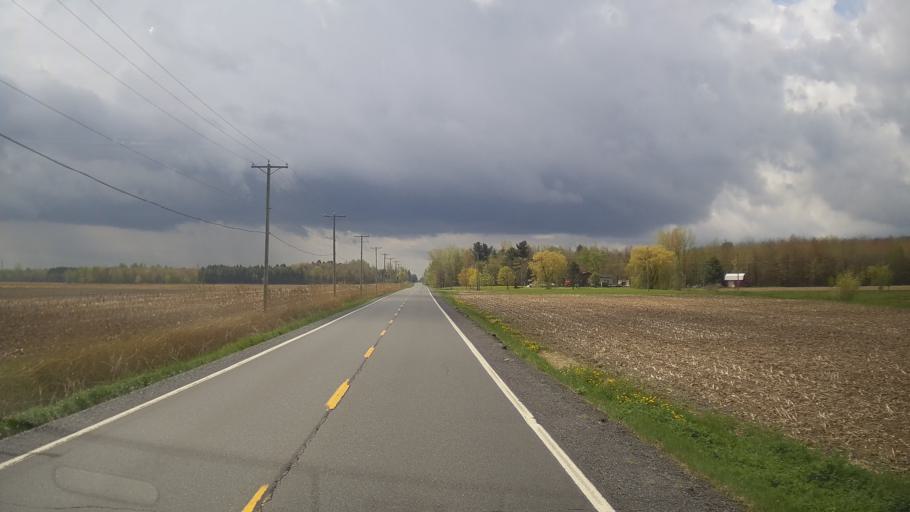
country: CA
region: Quebec
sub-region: Monteregie
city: Rougemont
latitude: 45.3464
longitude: -73.1061
